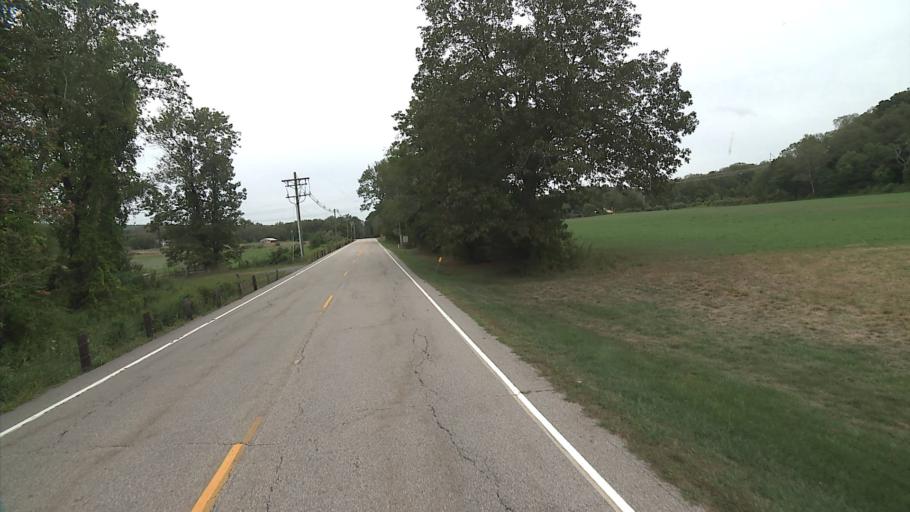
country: US
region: Connecticut
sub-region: Middlesex County
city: Essex Village
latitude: 41.4233
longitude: -72.3346
